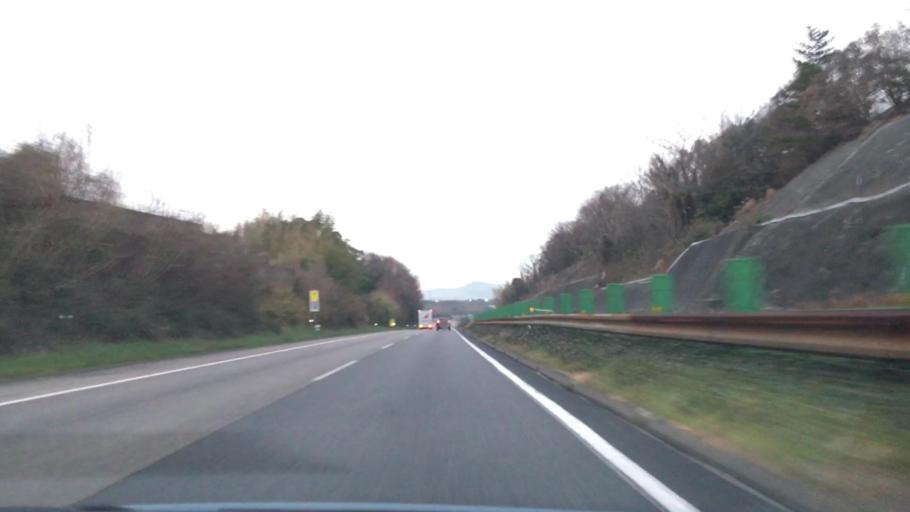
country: JP
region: Aichi
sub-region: Tokai-shi
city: Toyokawa
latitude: 34.8434
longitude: 137.4435
